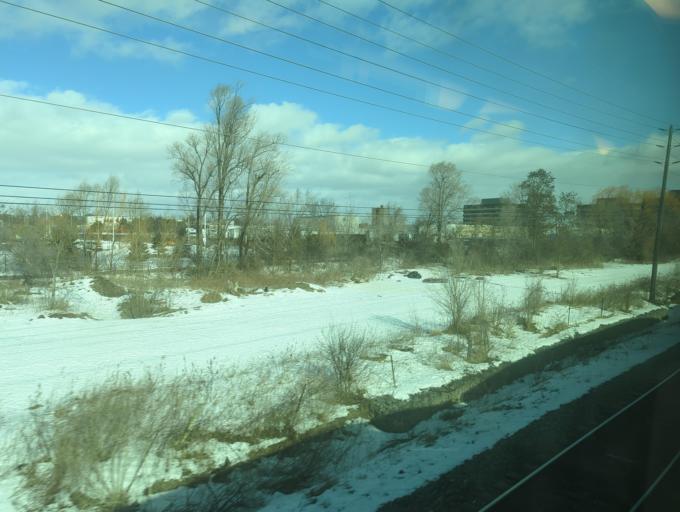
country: CA
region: Ontario
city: Oakville
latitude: 43.4390
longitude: -79.6991
